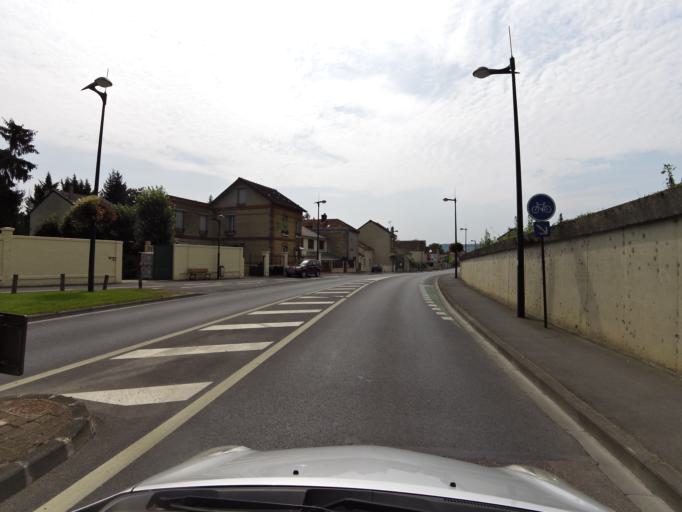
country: FR
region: Champagne-Ardenne
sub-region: Departement de la Marne
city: Pierry
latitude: 49.0311
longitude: 3.9483
